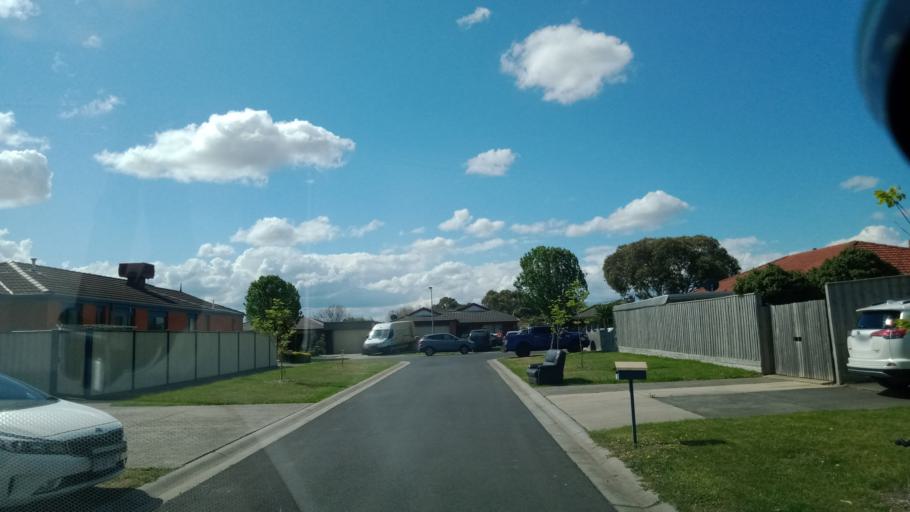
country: AU
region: Victoria
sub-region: Casey
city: Cranbourne West
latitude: -38.0998
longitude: 145.2604
